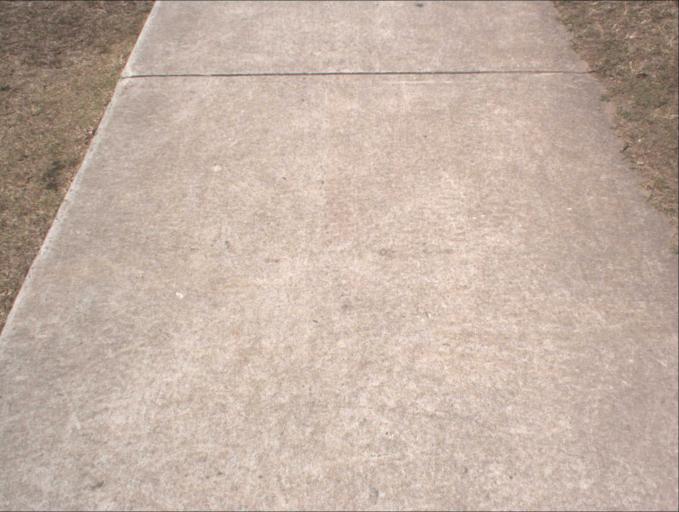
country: AU
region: Queensland
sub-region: Logan
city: Springwood
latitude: -27.6004
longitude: 153.1461
